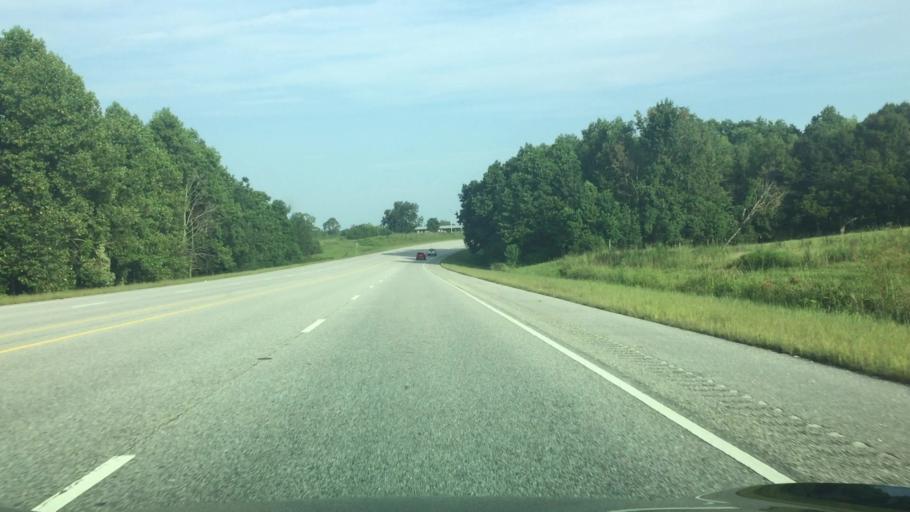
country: US
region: Alabama
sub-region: Butler County
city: Georgiana
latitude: 31.5180
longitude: -86.7097
